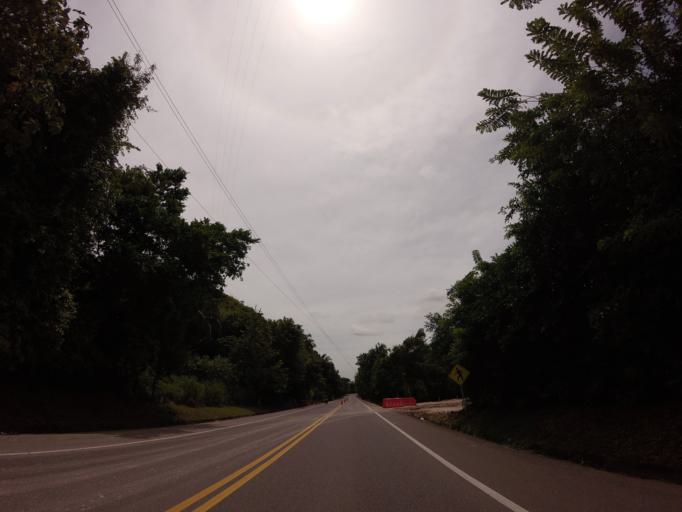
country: CO
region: Caldas
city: La Dorada
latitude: 5.4183
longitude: -74.6868
